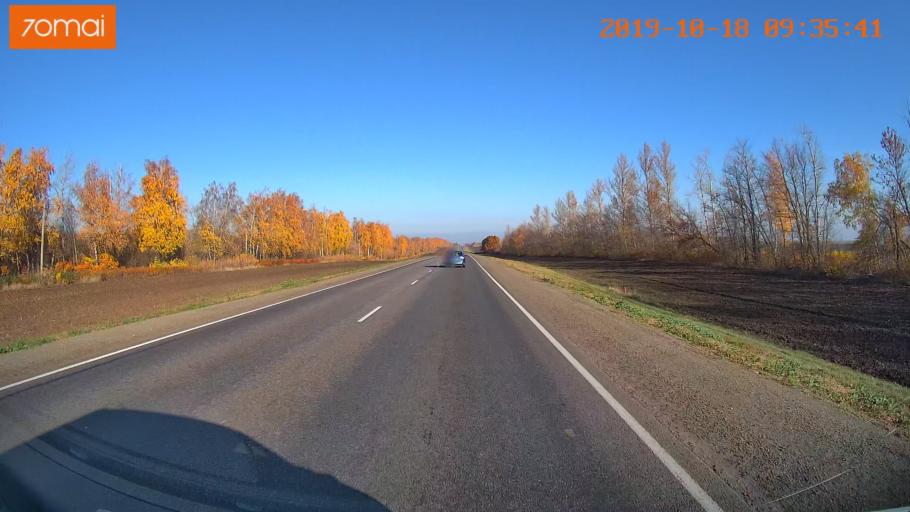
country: RU
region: Tula
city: Yefremov
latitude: 53.1956
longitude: 38.1478
